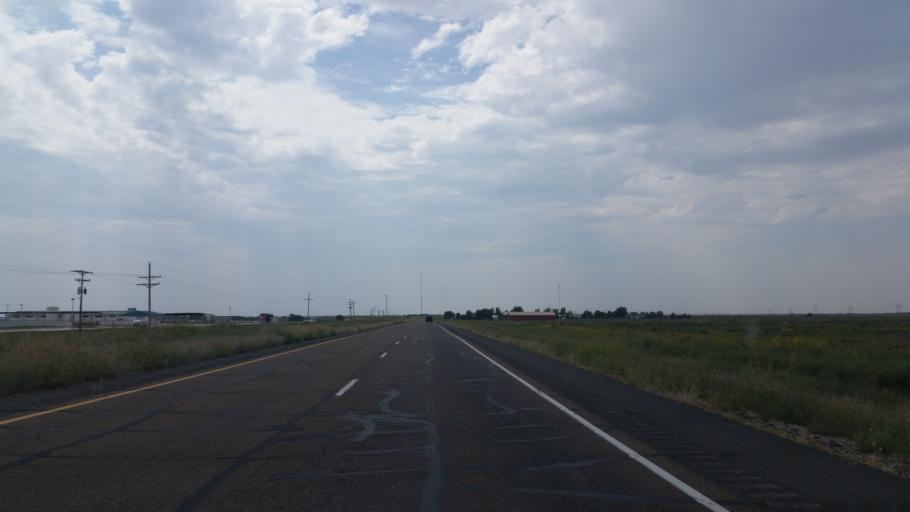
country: US
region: New Mexico
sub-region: Curry County
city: Clovis
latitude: 34.2799
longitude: -103.2167
